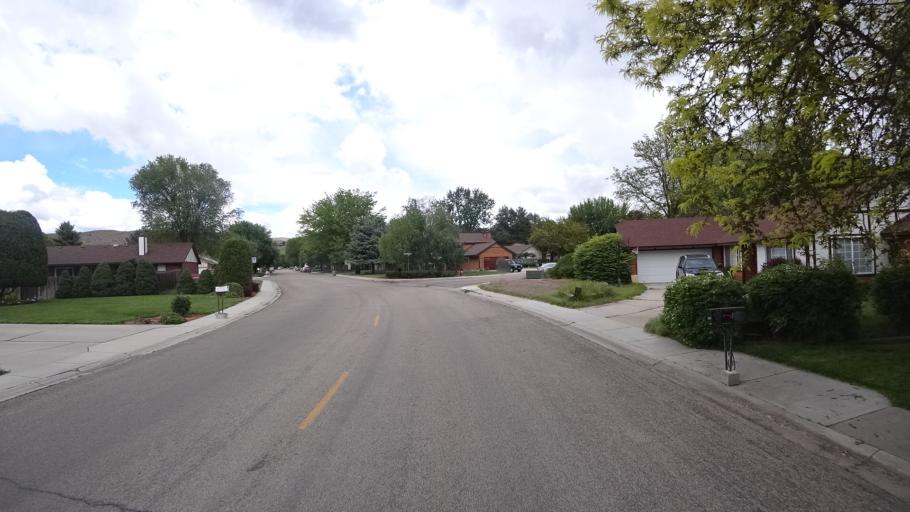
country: US
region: Idaho
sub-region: Ada County
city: Garden City
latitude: 43.6597
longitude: -116.2582
